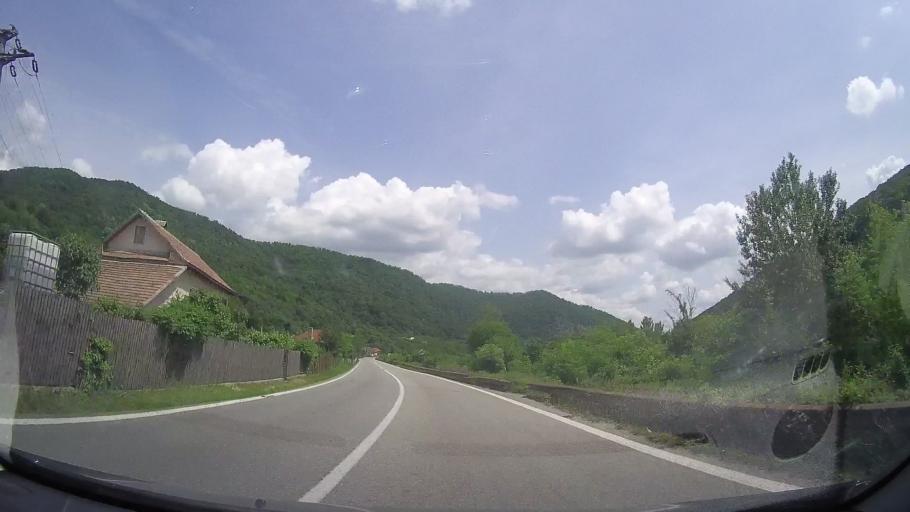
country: RO
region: Valcea
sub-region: Oras Calimanesti
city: Calimanesti
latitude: 45.2619
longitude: 24.3255
